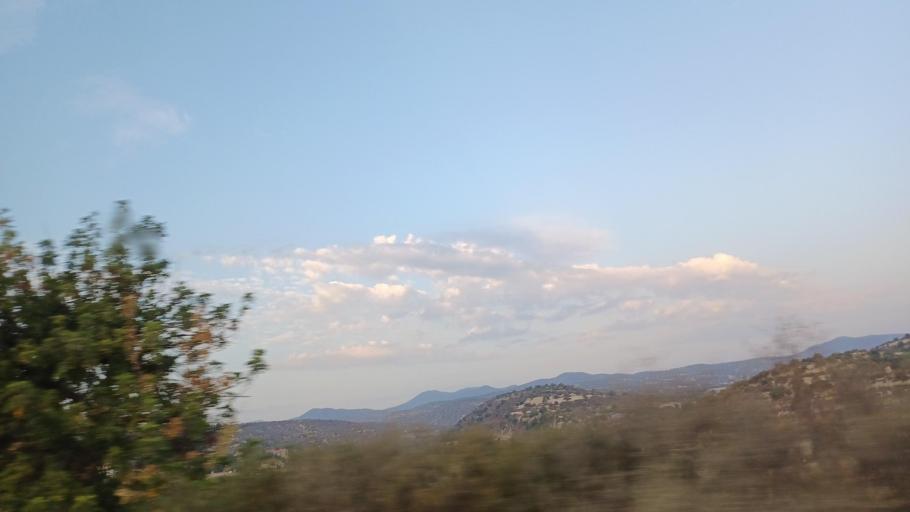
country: CY
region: Limassol
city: Pano Polemidia
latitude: 34.7551
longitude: 32.9717
